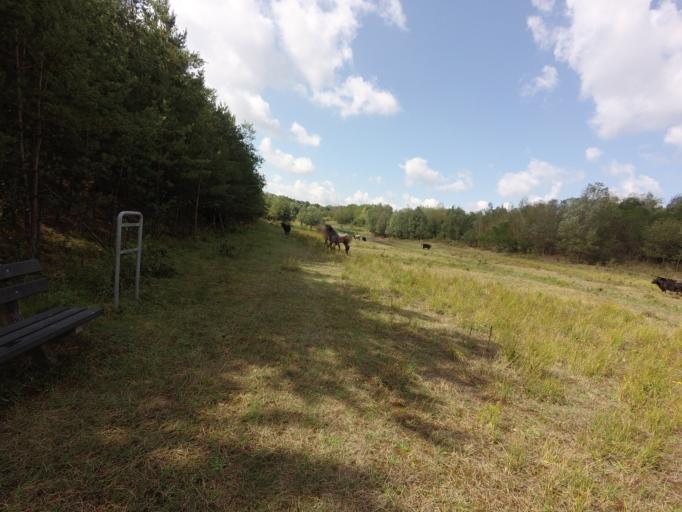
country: NL
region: Limburg
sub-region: Gemeente Brunssum
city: Brunssum
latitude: 50.9303
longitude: 6.0309
